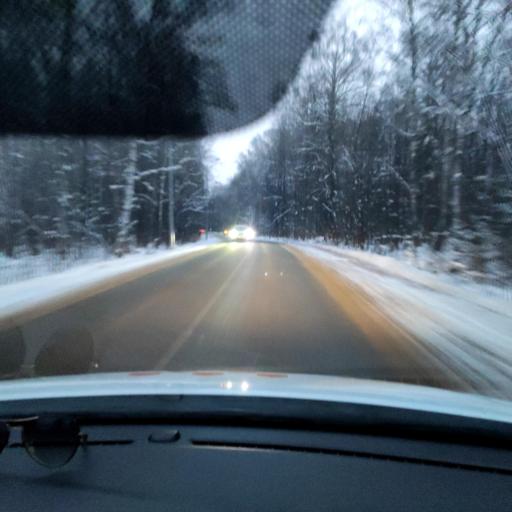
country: RU
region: Tatarstan
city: Vysokaya Gora
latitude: 55.9305
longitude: 49.1625
